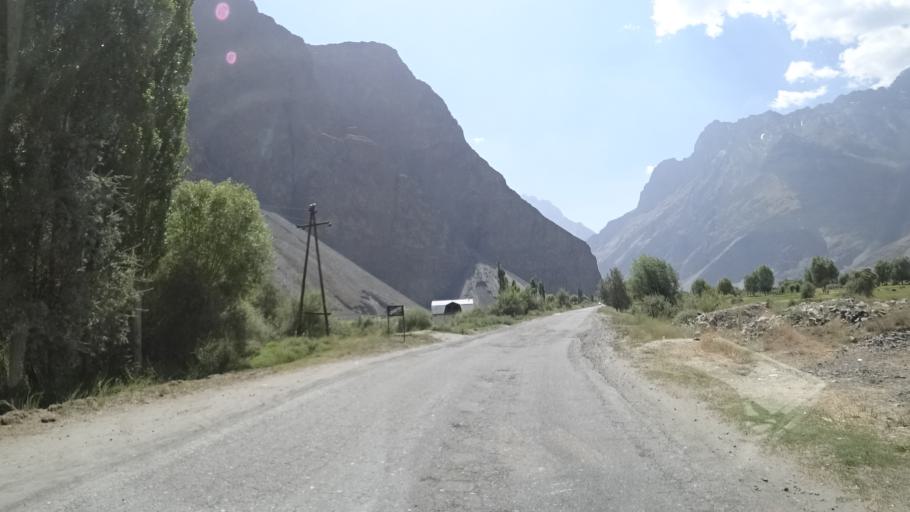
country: TJ
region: Gorno-Badakhshan
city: Rushon
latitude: 37.9613
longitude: 71.5321
